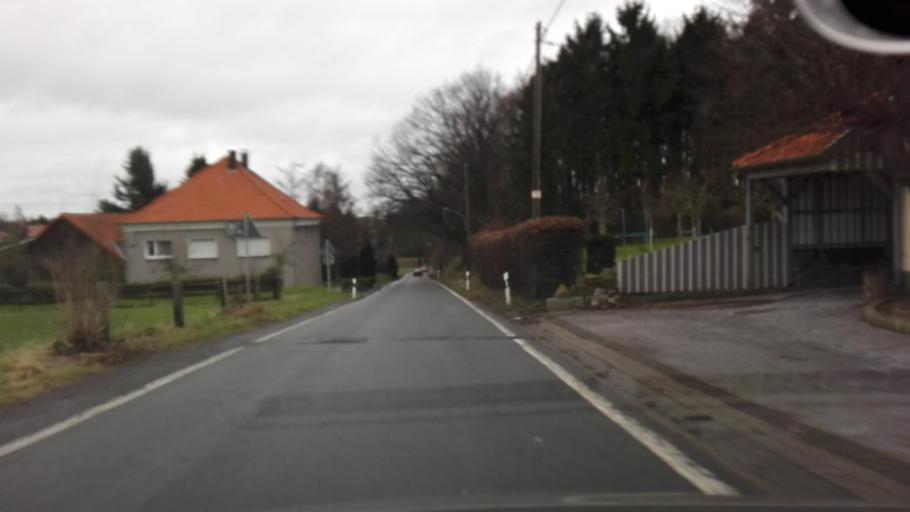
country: DE
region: North Rhine-Westphalia
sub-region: Regierungsbezirk Arnsberg
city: Unna
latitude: 51.5155
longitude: 7.7271
